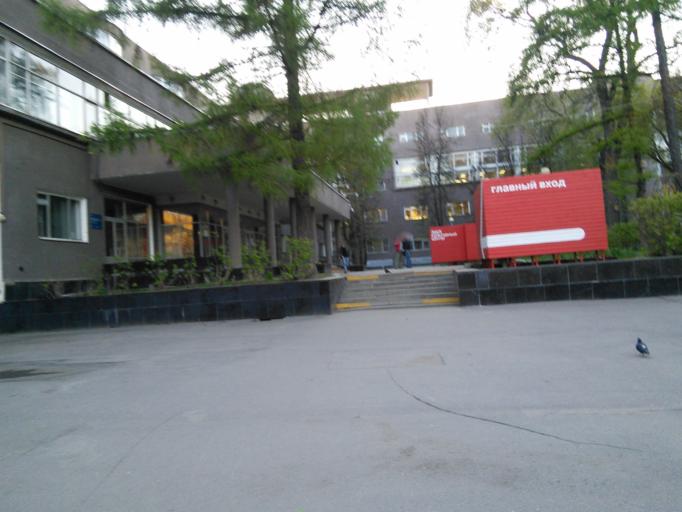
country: RU
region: Moskovskaya
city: Kozhukhovo
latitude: 55.7145
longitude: 37.6584
